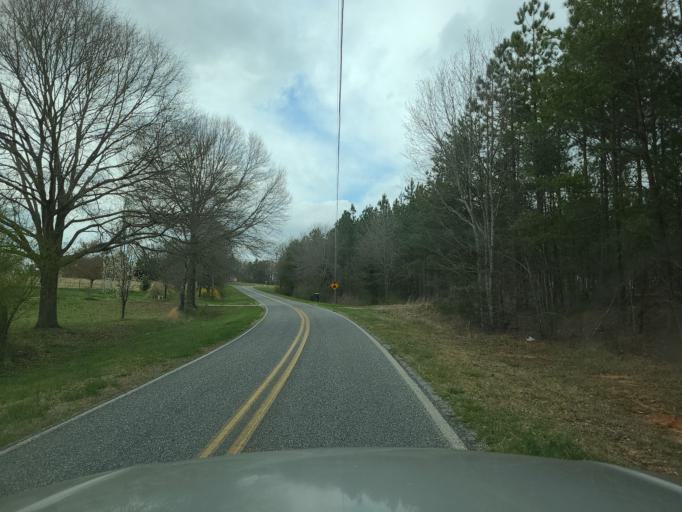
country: US
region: North Carolina
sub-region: Cleveland County
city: Boiling Springs
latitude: 35.2460
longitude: -81.7166
